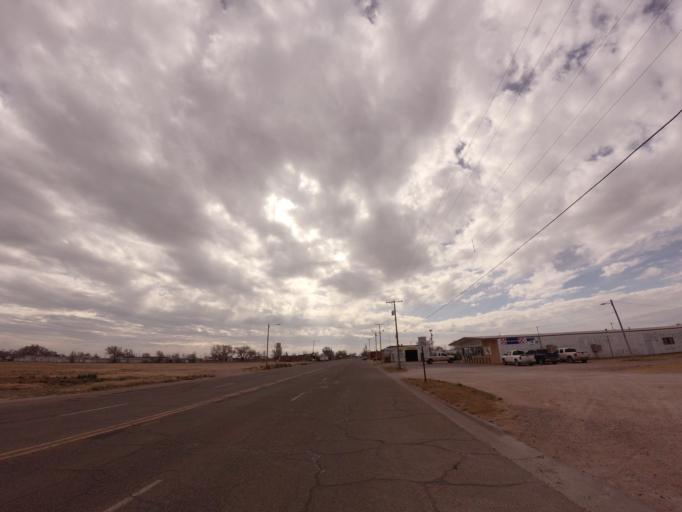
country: US
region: New Mexico
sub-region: Curry County
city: Clovis
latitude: 34.3952
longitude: -103.2206
